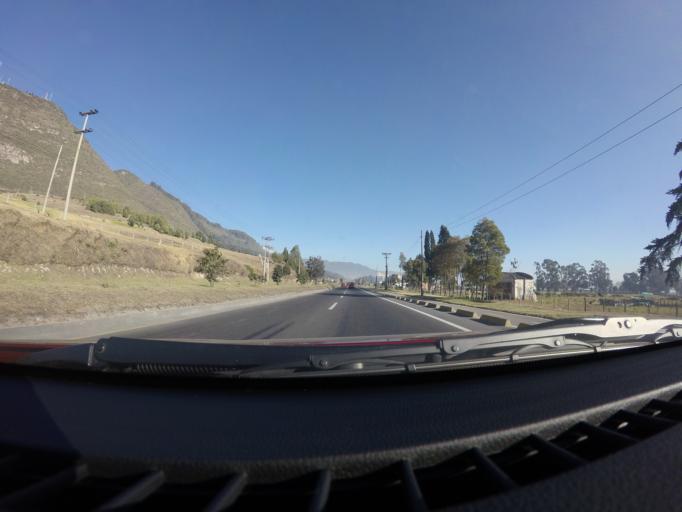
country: CO
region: Cundinamarca
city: Zipaquira
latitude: 4.9776
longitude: -74.0033
